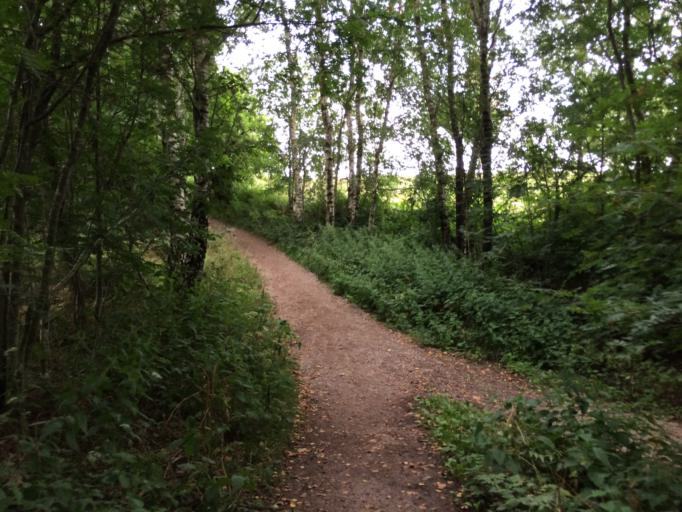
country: DK
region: Central Jutland
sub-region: Syddjurs Kommune
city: Ronde
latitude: 56.2288
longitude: 10.5345
